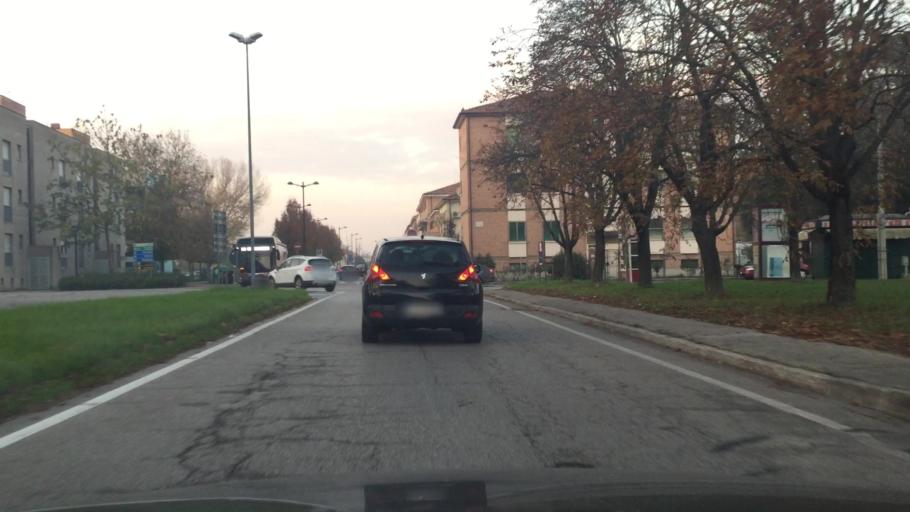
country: IT
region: Emilia-Romagna
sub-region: Provincia di Ferrara
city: Ferrara
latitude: 44.8608
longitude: 11.6076
